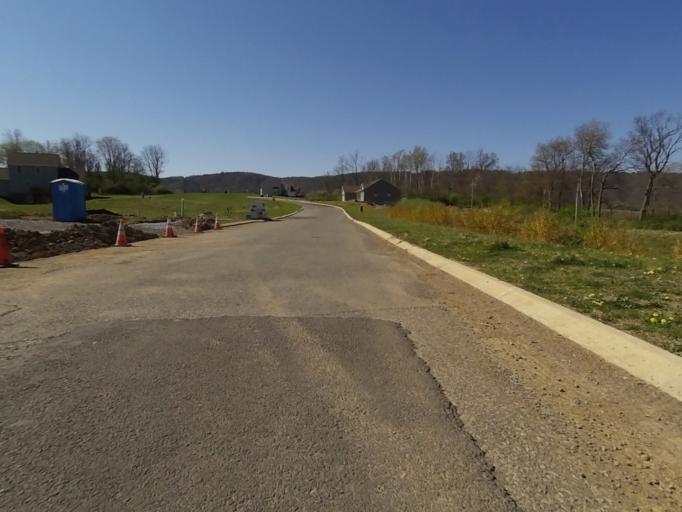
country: US
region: Pennsylvania
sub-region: Centre County
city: Houserville
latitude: 40.8798
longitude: -77.8301
